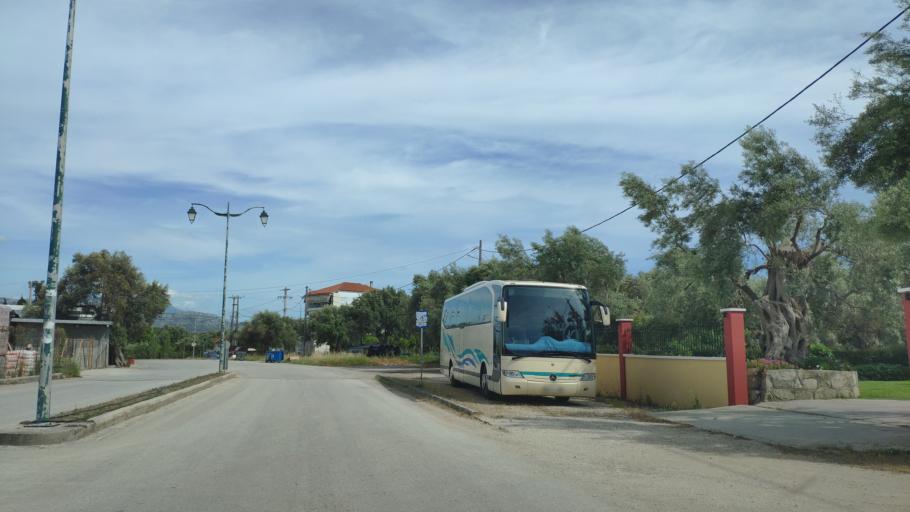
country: GR
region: Ionian Islands
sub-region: Lefkada
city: Lefkada
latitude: 38.8232
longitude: 20.7001
